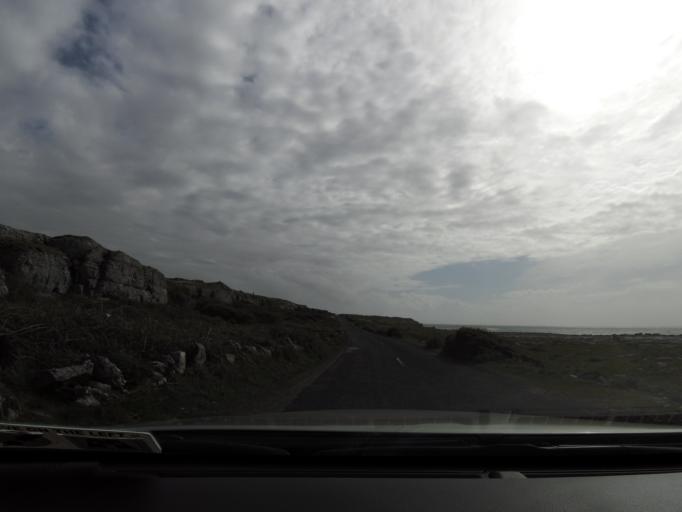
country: IE
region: Connaught
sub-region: County Galway
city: Bearna
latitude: 53.0647
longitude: -9.3597
